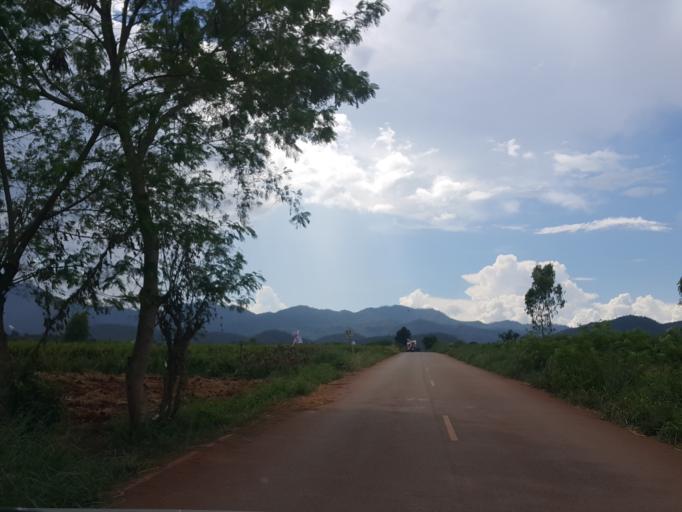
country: TH
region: Chiang Mai
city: Phrao
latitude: 19.3345
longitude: 99.1698
